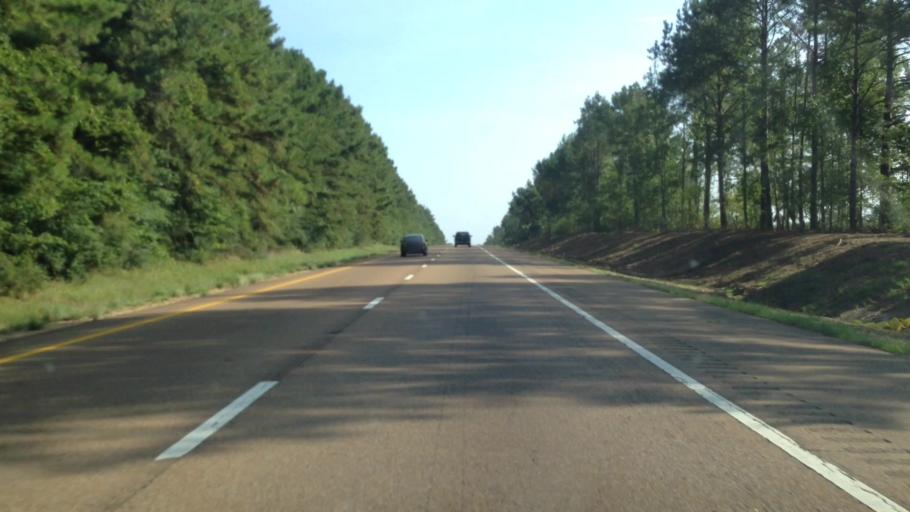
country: US
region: Mississippi
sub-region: Lincoln County
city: Brookhaven
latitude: 31.4633
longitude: -90.4788
